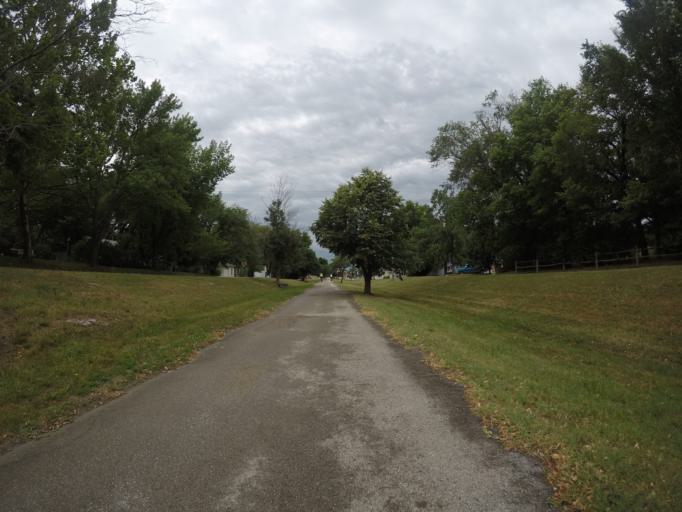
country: US
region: Kansas
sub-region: Anderson County
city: Garnett
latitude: 38.2829
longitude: -95.2401
